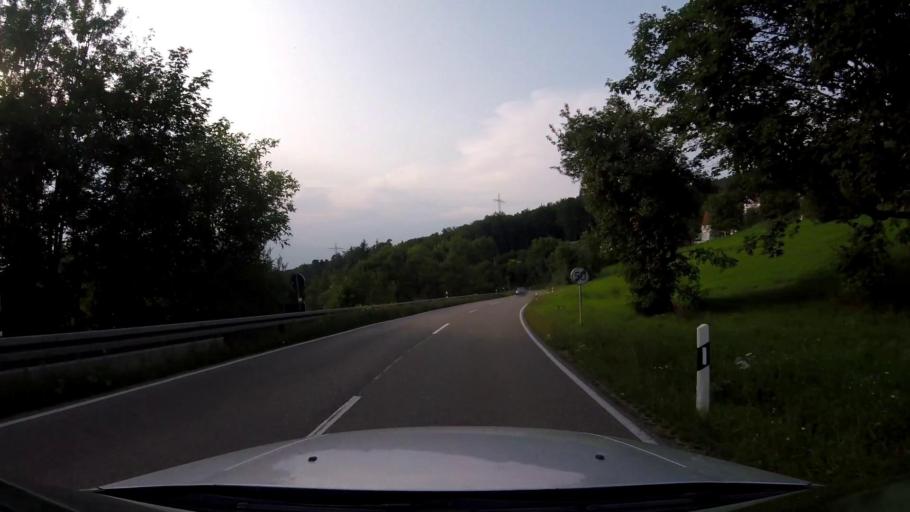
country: DE
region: Baden-Wuerttemberg
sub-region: Regierungsbezirk Stuttgart
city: Urbach
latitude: 48.8564
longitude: 9.5903
